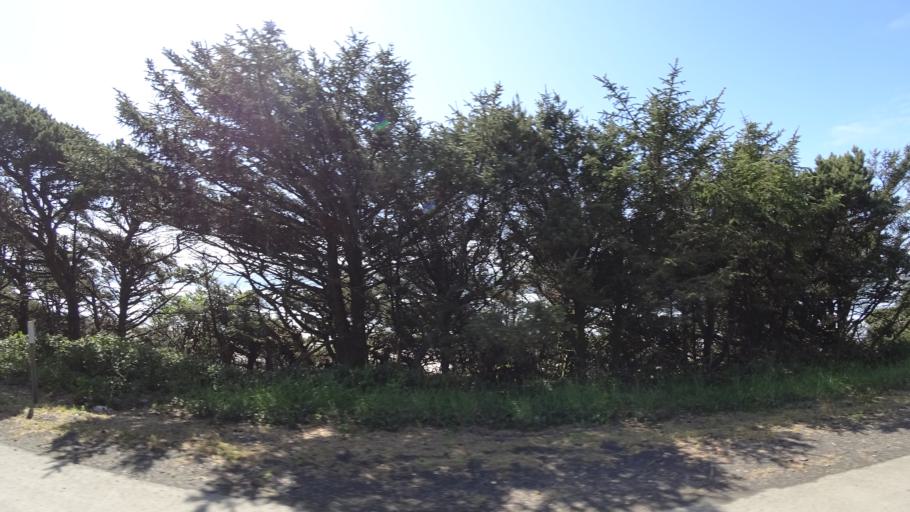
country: US
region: Oregon
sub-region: Lincoln County
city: Depoe Bay
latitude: 44.7347
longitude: -124.0567
